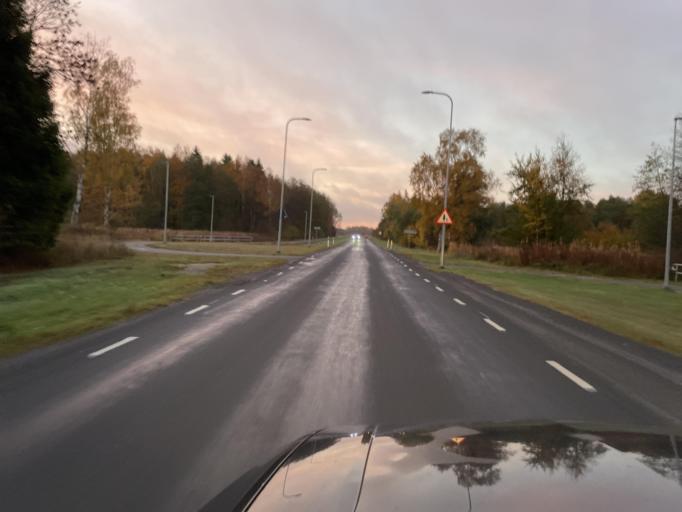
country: EE
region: Harju
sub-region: Nissi vald
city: Riisipere
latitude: 59.2439
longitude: 24.2431
